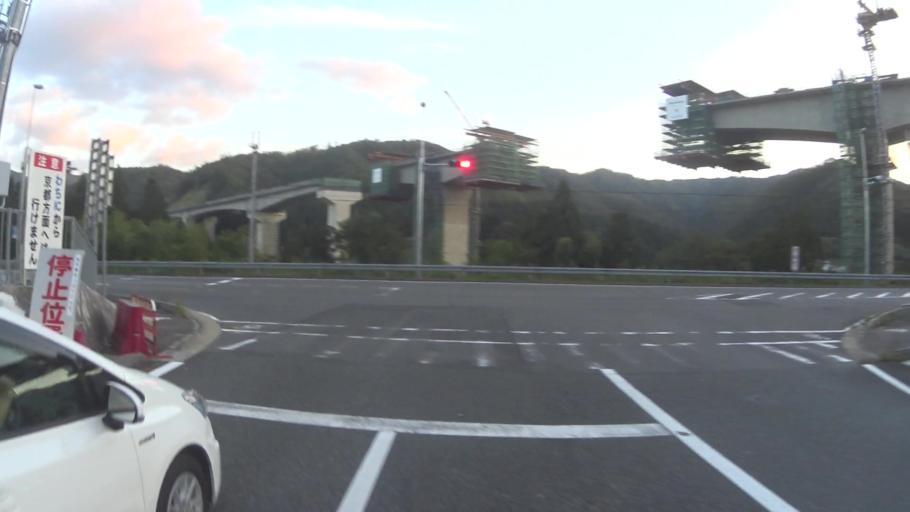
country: JP
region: Kyoto
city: Ayabe
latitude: 35.2764
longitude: 135.3399
